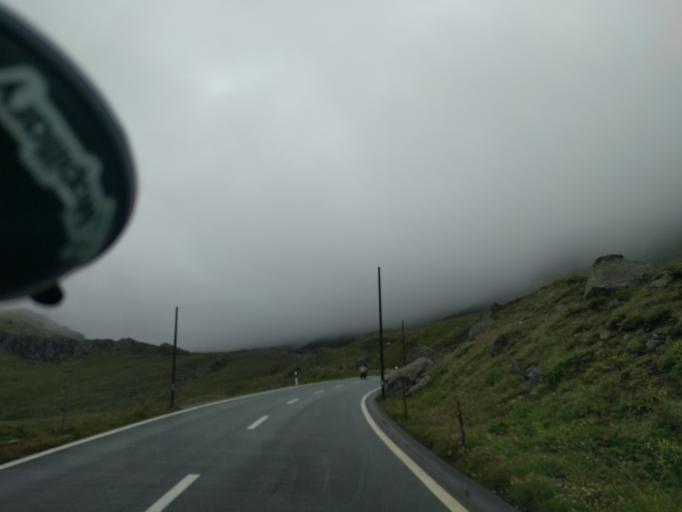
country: CH
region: Grisons
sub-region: Praettigau/Davos District
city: Davos
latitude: 46.7596
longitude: 9.9401
